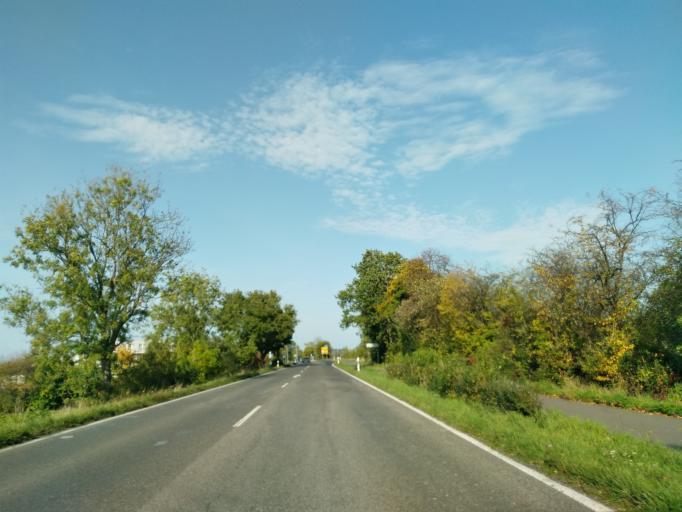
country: DE
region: North Rhine-Westphalia
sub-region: Regierungsbezirk Koln
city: Bad Honnef
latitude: 50.6941
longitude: 7.2780
